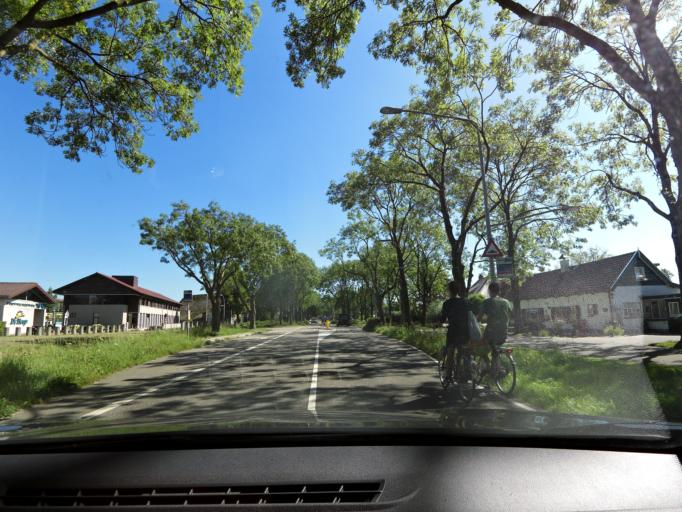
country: NL
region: South Holland
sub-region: Gemeente Dordrecht
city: Dordrecht
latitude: 51.7940
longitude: 4.7185
